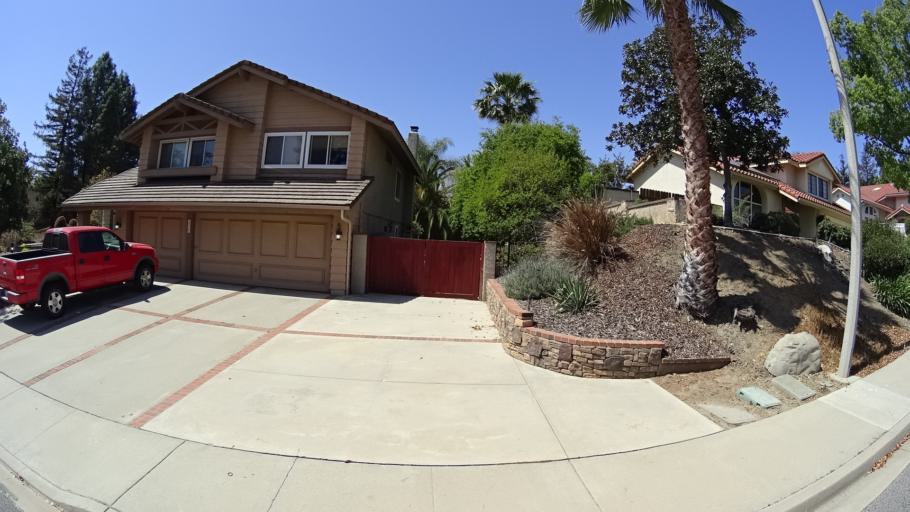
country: US
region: California
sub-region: Ventura County
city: Casa Conejo
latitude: 34.2062
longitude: -118.8913
